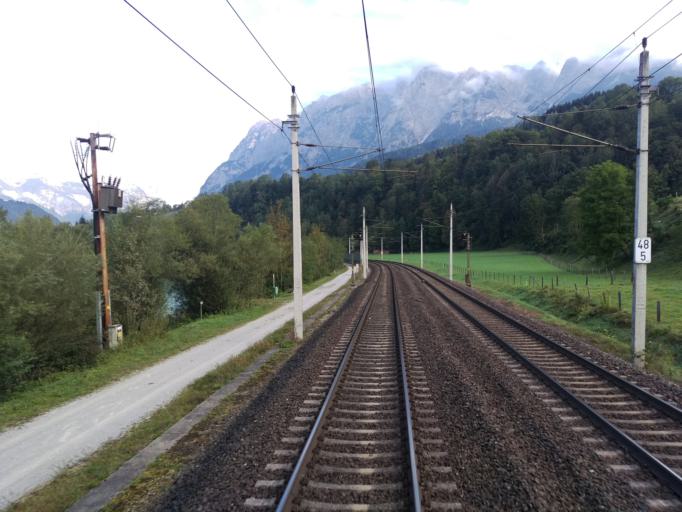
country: AT
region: Salzburg
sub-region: Politischer Bezirk Sankt Johann im Pongau
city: Pfarrwerfen
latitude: 47.4483
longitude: 13.2135
